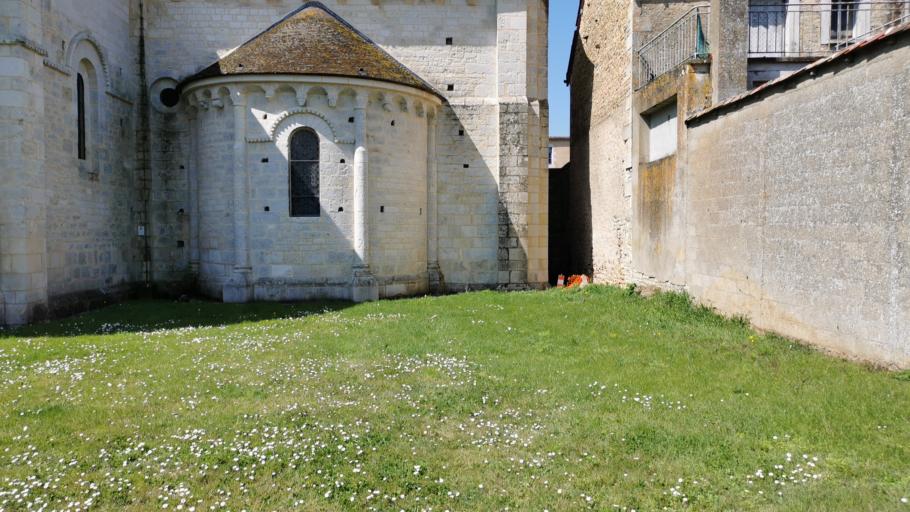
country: FR
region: Poitou-Charentes
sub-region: Departement de la Vienne
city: Civray
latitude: 46.1483
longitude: 0.2973
